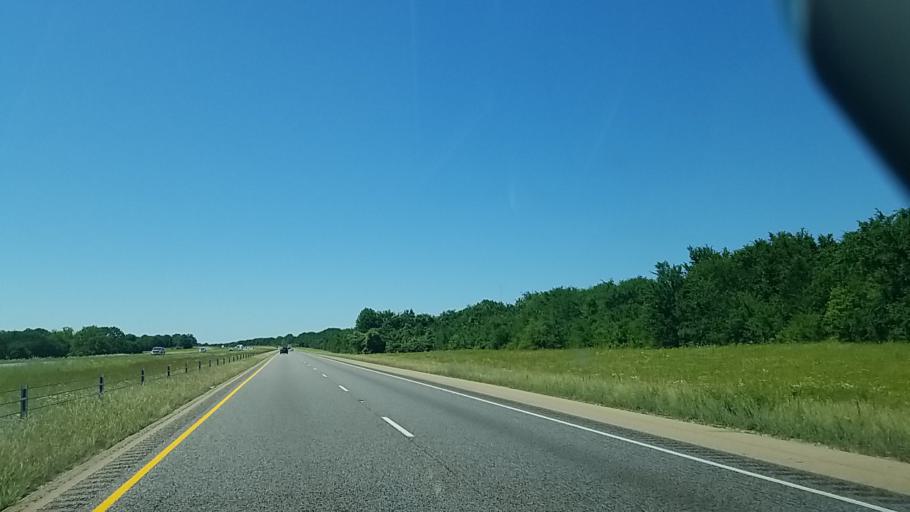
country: US
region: Texas
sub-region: Freestone County
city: Fairfield
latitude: 31.6819
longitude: -96.1650
